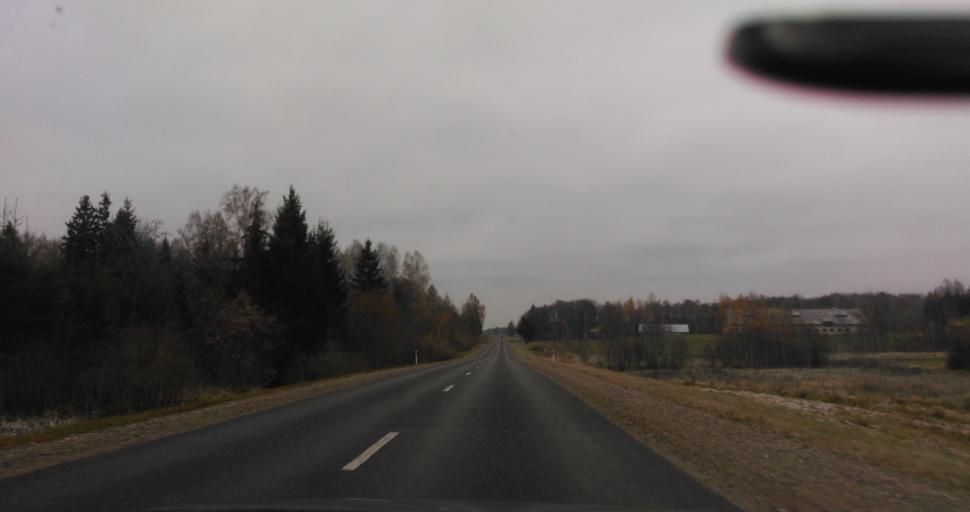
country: LT
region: Panevezys
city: Rokiskis
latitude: 55.8895
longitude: 25.5482
